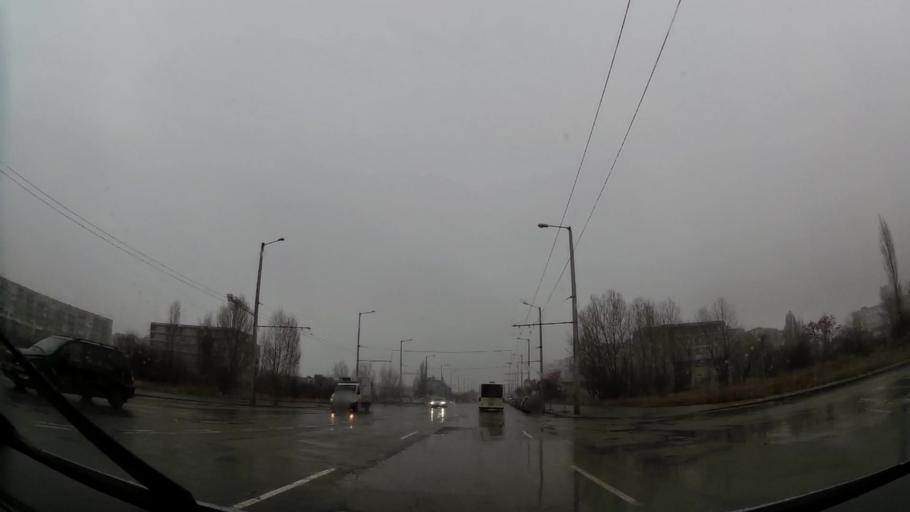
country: BG
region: Sofia-Capital
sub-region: Stolichna Obshtina
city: Sofia
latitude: 42.6566
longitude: 23.3963
